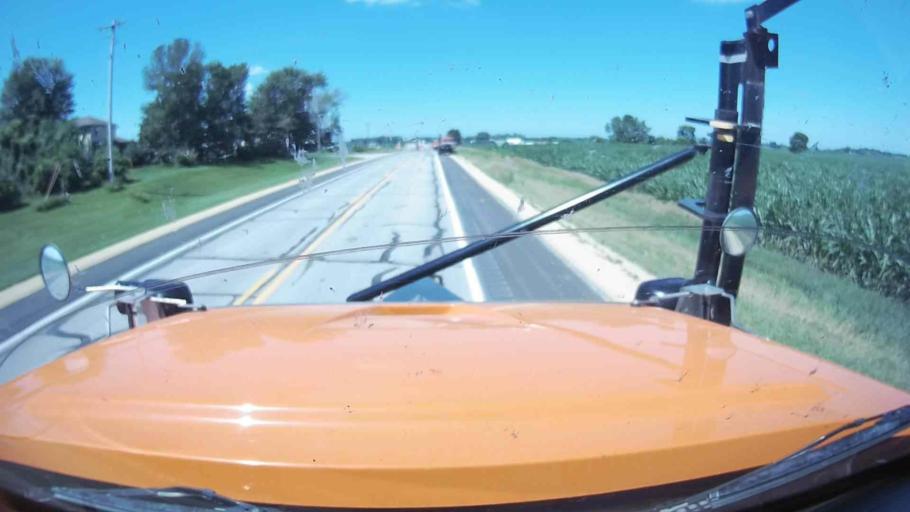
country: US
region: Iowa
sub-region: Worth County
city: Manly
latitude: 43.2842
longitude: -93.0974
